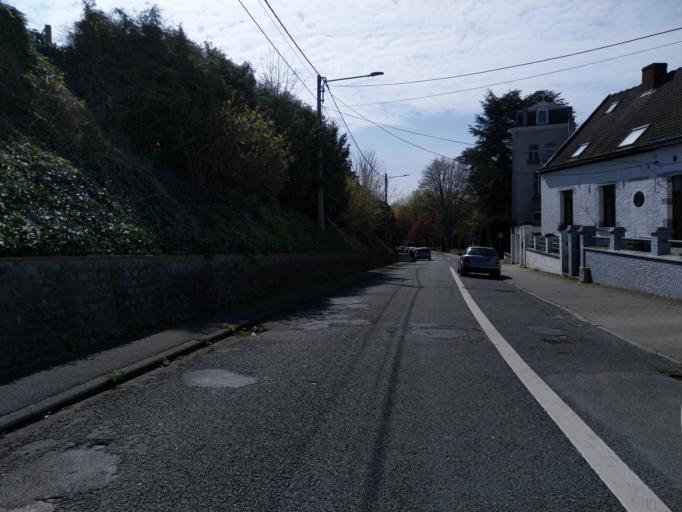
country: BE
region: Wallonia
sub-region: Province du Hainaut
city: Mons
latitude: 50.4724
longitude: 4.0092
